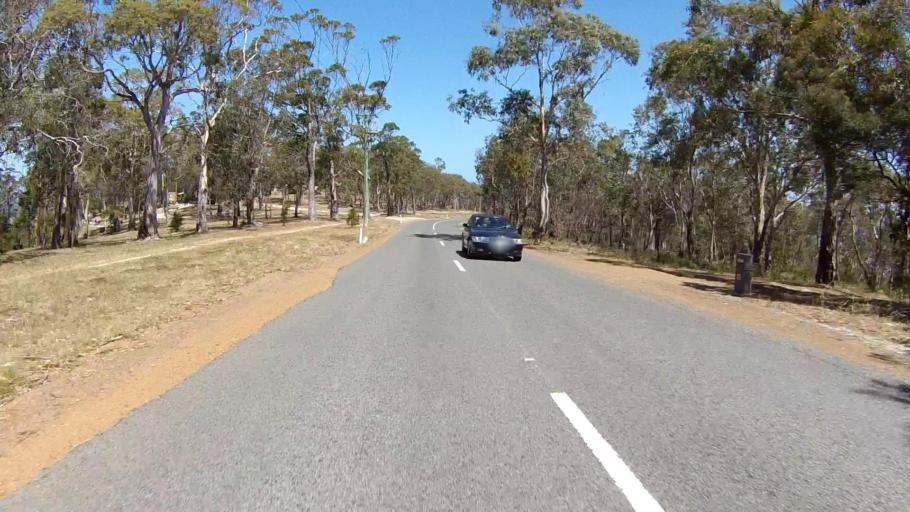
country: AU
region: Tasmania
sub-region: Clarence
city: Sandford
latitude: -43.0180
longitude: 147.4819
